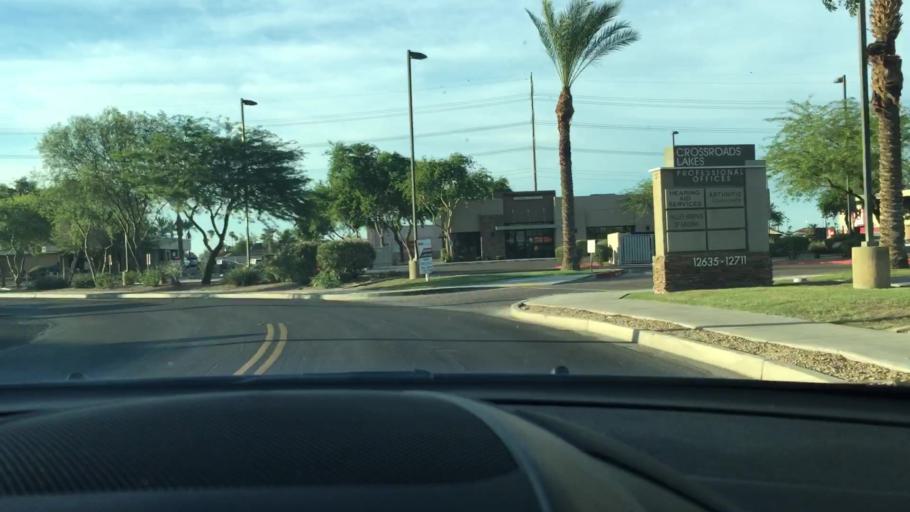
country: US
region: Arizona
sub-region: Maricopa County
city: Surprise
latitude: 33.6368
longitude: -112.3334
